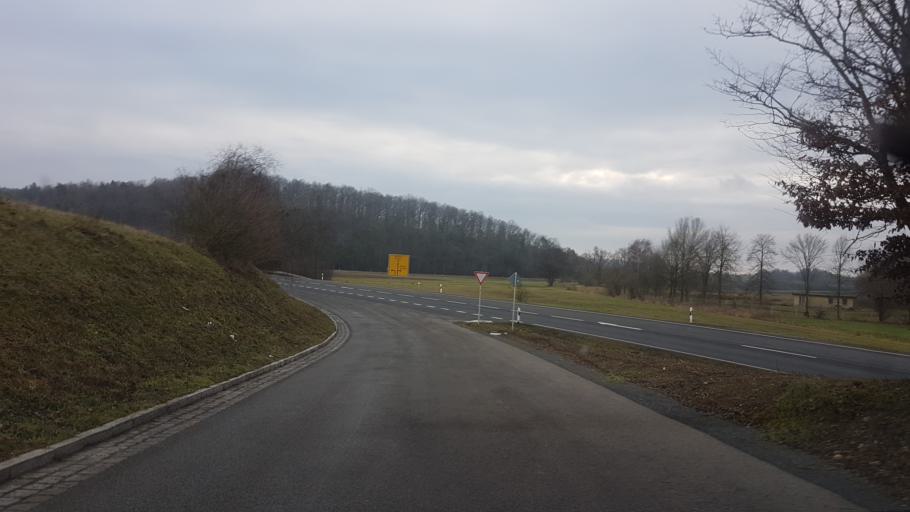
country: DE
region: Bavaria
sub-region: Regierungsbezirk Unterfranken
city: Ermershausen
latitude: 50.2312
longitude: 10.5695
